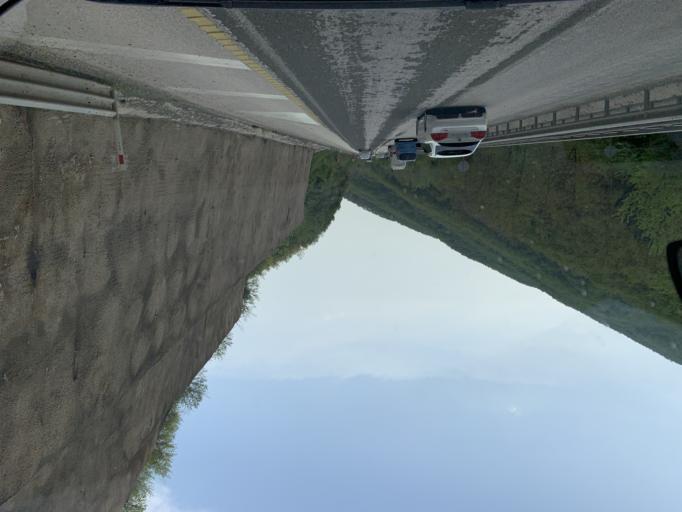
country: TR
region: Bursa
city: Kursunlu
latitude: 39.9989
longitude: 29.6533
